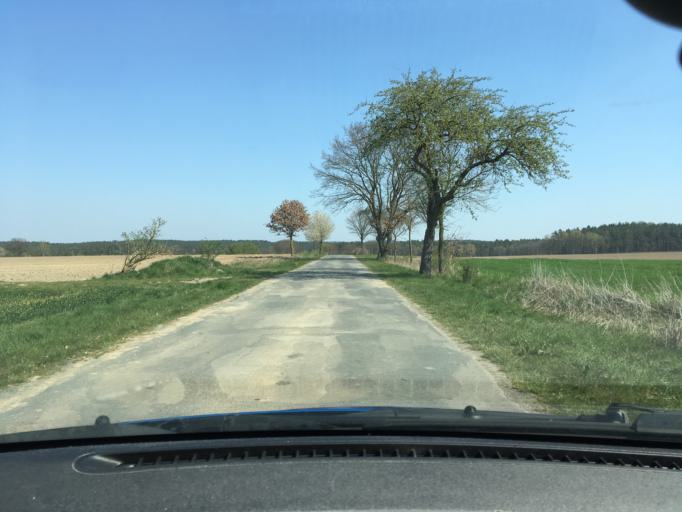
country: DE
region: Lower Saxony
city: Reinstorf
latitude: 53.2002
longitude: 10.5922
